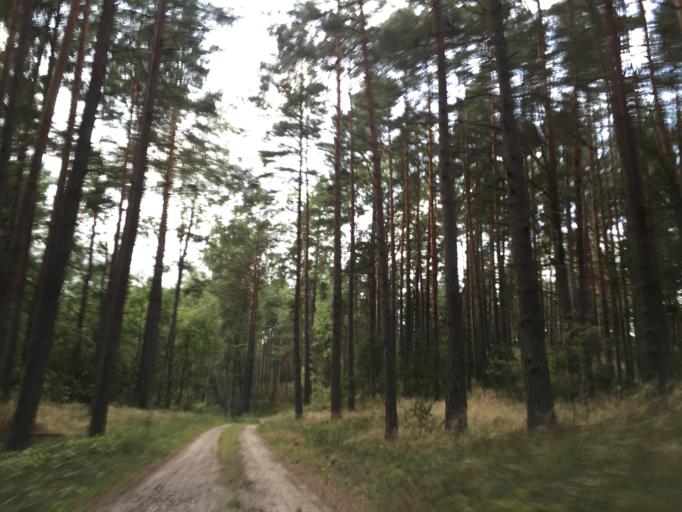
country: LV
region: Jurmala
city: Jurmala
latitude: 56.8711
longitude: 23.7097
